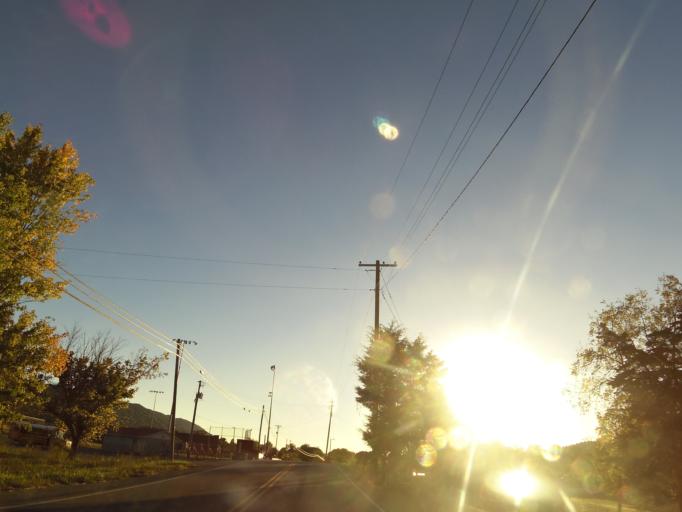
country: US
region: Tennessee
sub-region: Grainger County
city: Rutledge
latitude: 36.2954
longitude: -83.5884
